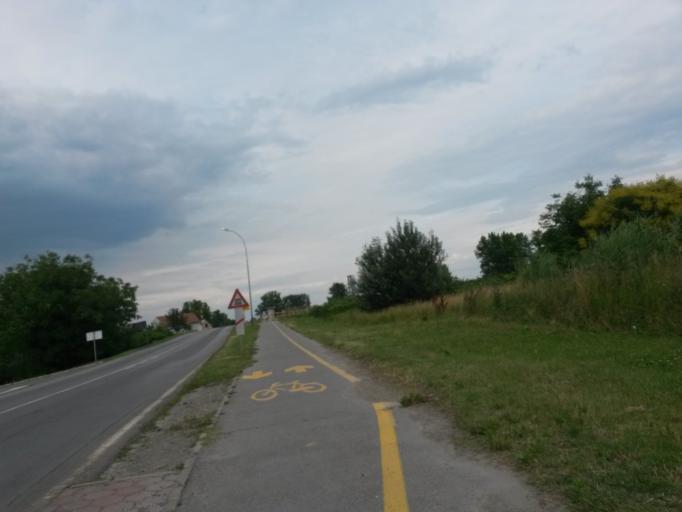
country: HR
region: Osjecko-Baranjska
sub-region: Grad Osijek
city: Osijek
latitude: 45.5670
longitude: 18.7061
